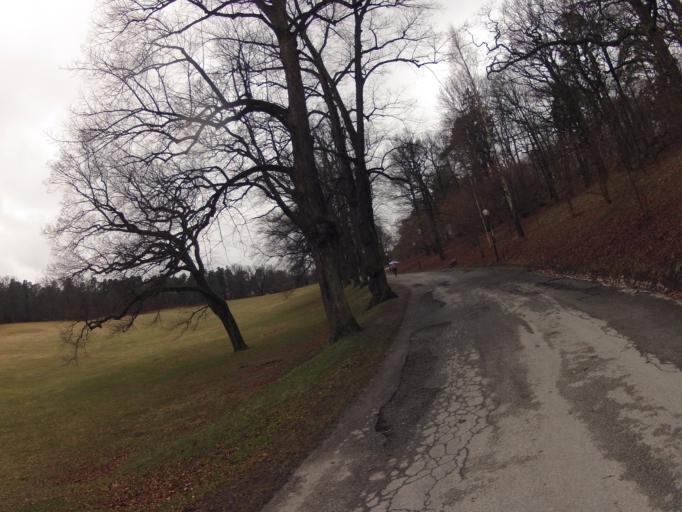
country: SE
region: Stockholm
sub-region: Norrtalje Kommun
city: Bergshamra
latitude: 59.3635
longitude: 18.0353
